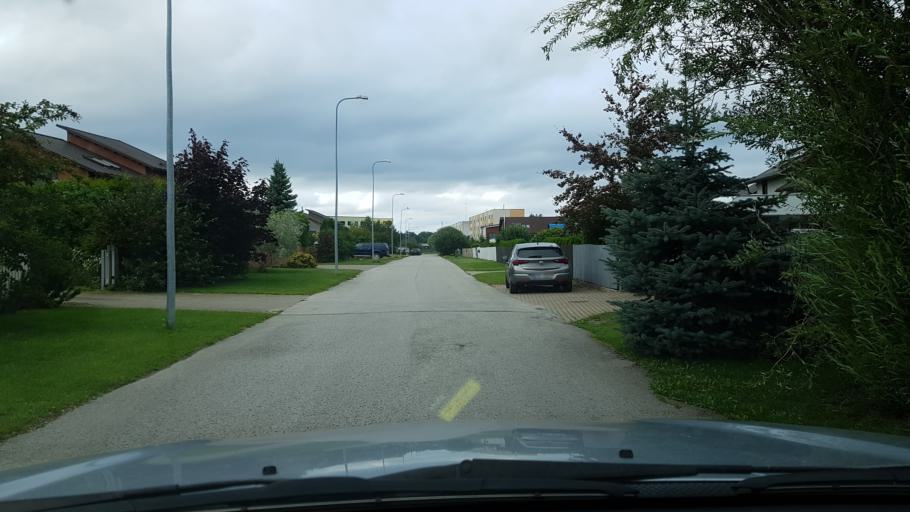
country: EE
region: Harju
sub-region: Tallinna linn
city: Tallinn
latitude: 59.4028
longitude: 24.8220
